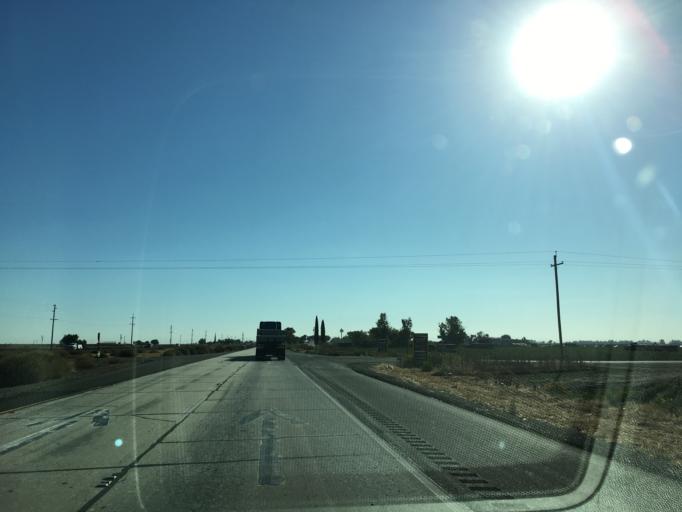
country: US
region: California
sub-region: Merced County
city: Dos Palos
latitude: 37.0541
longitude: -120.6730
